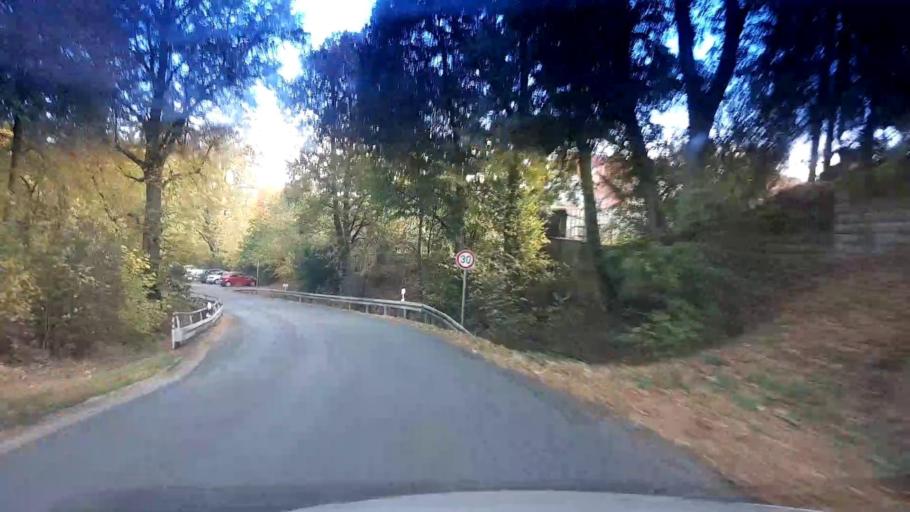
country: DE
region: Bavaria
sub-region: Upper Franconia
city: Altenkunstadt
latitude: 50.1226
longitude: 11.2505
